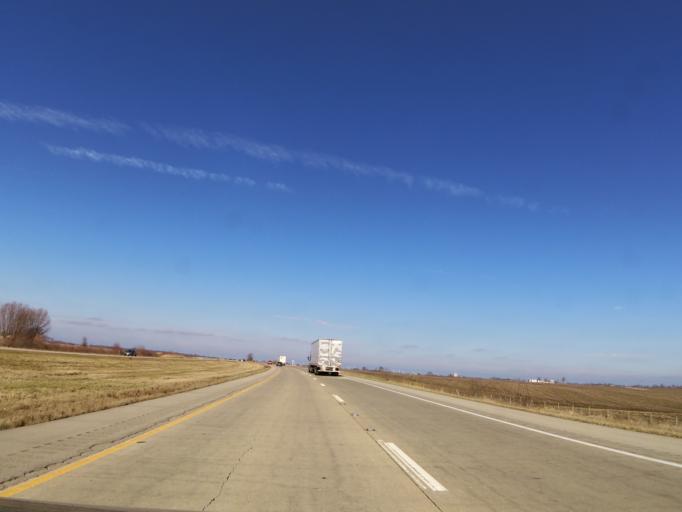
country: US
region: Illinois
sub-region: LaSalle County
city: Mendota
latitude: 41.5128
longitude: -89.0525
